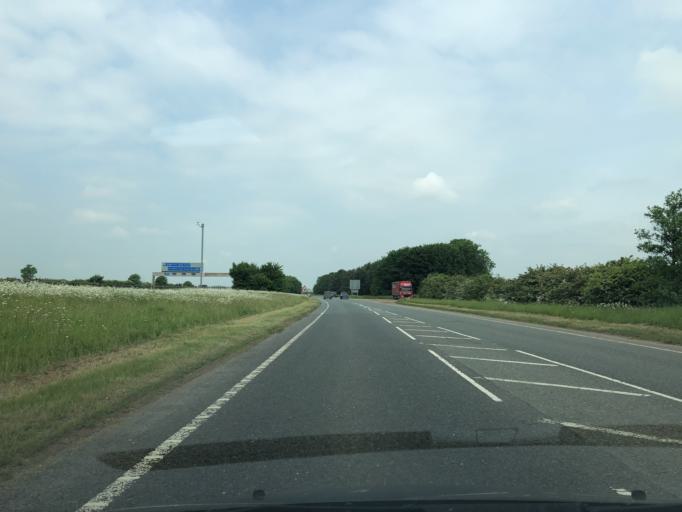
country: GB
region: England
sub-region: North Yorkshire
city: Boroughbridge
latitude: 54.1260
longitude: -1.4141
